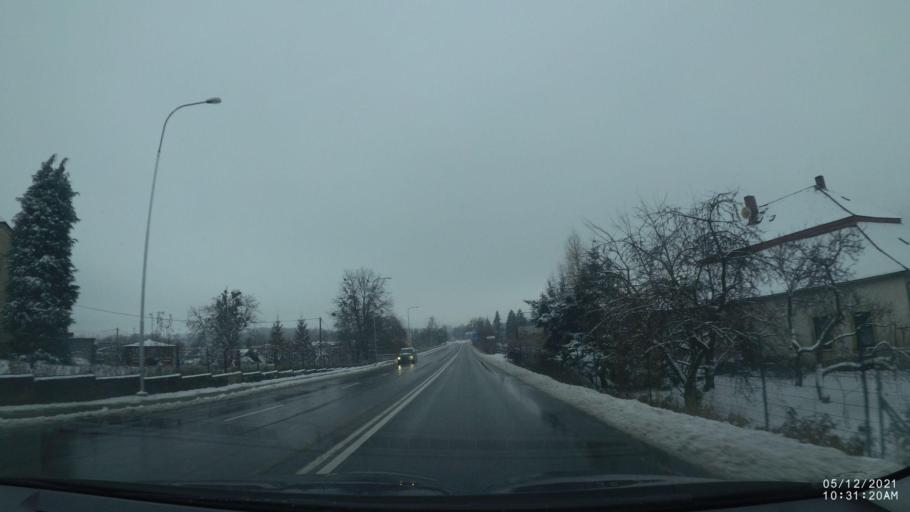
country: CZ
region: Kralovehradecky
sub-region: Okres Rychnov nad Kneznou
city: Rychnov nad Kneznou
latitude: 50.1515
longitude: 16.2826
